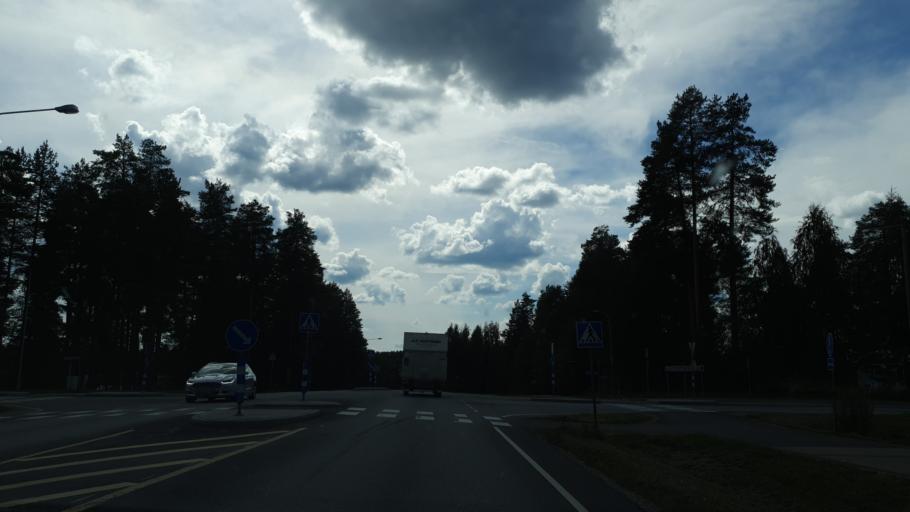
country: FI
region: Kainuu
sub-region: Kajaani
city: Sotkamo
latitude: 64.1383
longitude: 28.4128
